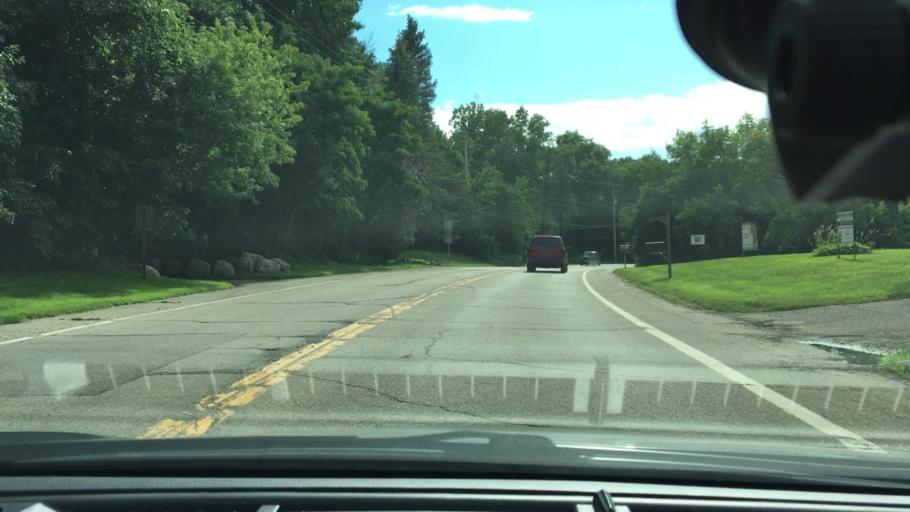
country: US
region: Minnesota
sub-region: Hennepin County
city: Mound
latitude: 44.9312
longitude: -93.6566
